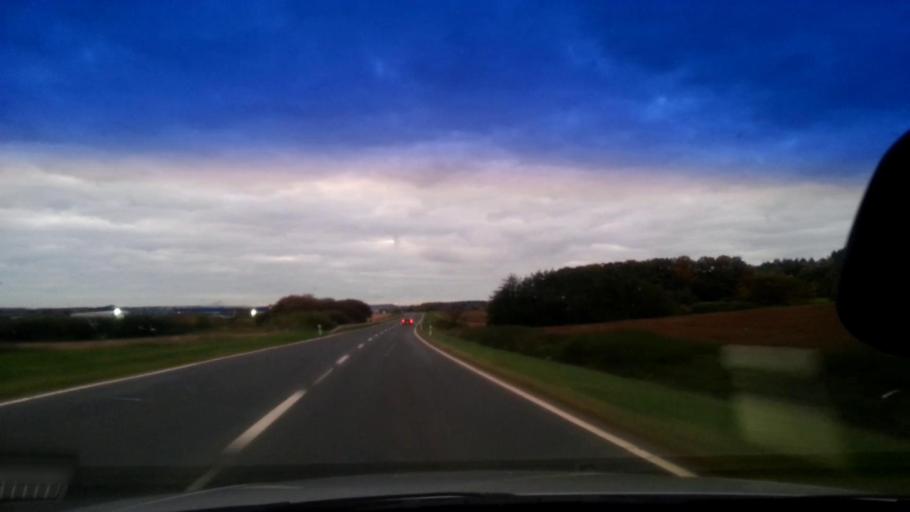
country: DE
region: Bavaria
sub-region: Upper Franconia
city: Schesslitz
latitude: 49.9797
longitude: 11.0565
